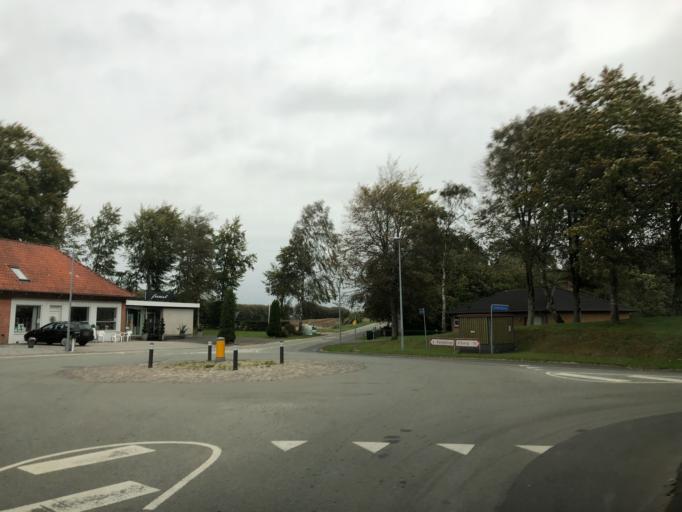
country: DK
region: Central Jutland
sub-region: Viborg Kommune
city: Viborg
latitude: 56.4127
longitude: 9.2853
